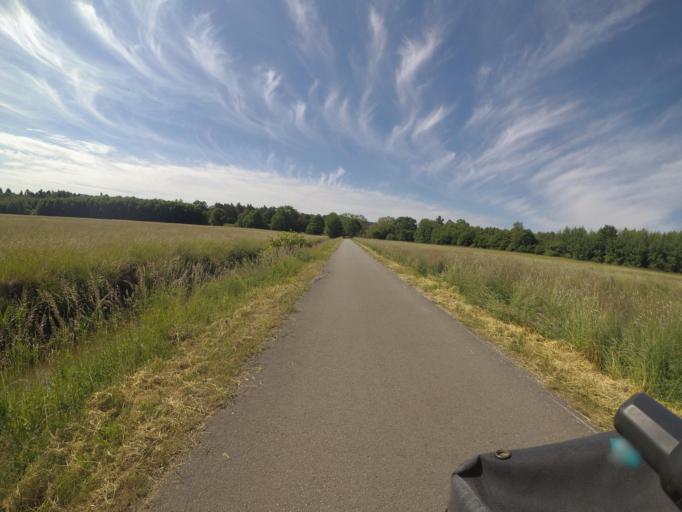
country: DE
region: Rheinland-Pfalz
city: Ramstein-Miesenbach
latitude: 49.4311
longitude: 7.5674
